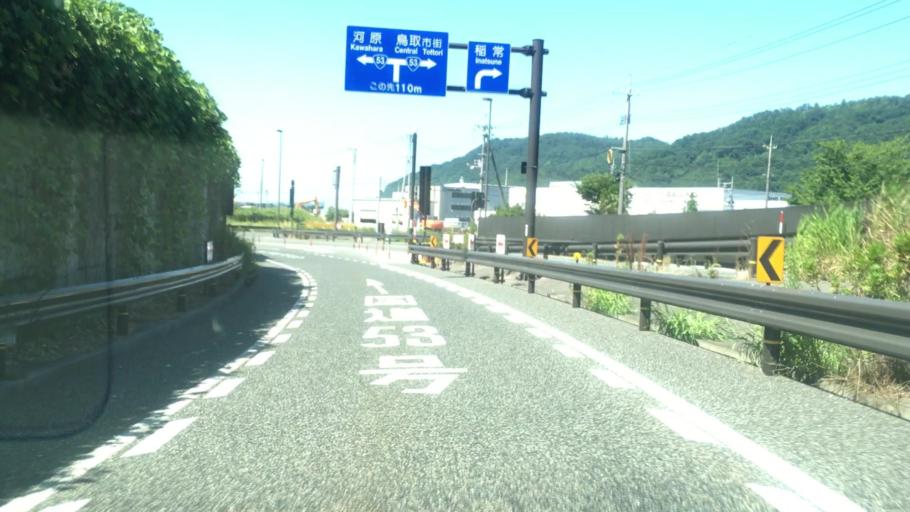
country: JP
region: Tottori
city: Tottori
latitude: 35.4236
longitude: 134.2075
